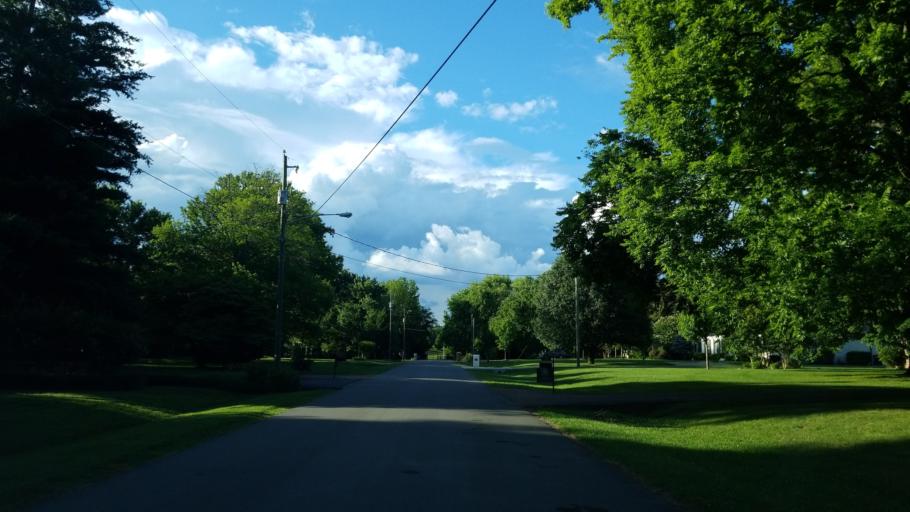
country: US
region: Tennessee
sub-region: Williamson County
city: Brentwood
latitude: 36.0276
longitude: -86.8150
